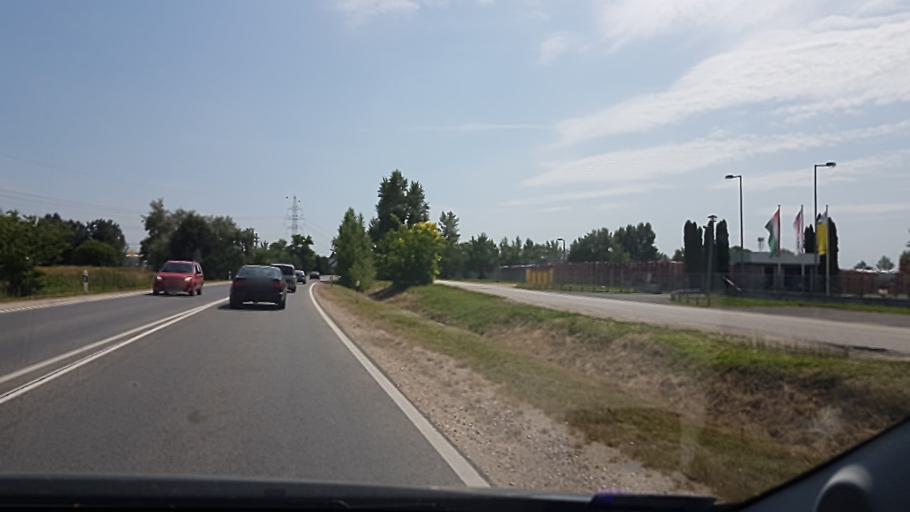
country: HU
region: Pest
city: Dunaharaszti
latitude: 47.3526
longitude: 19.1235
